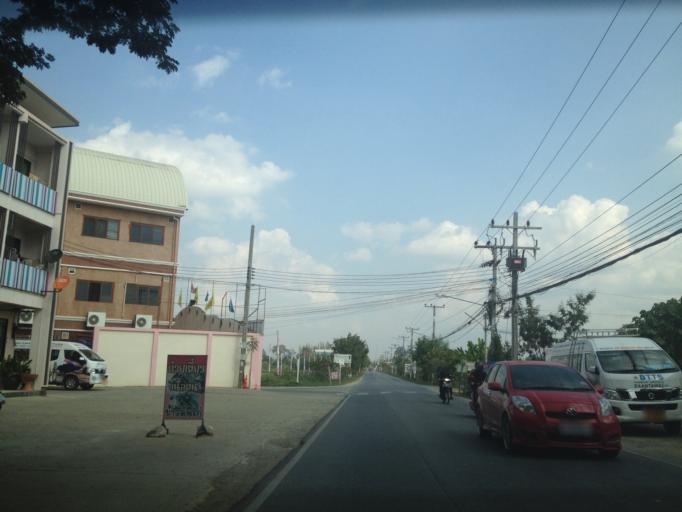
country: TH
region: Chiang Mai
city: Saraphi
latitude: 18.7070
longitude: 99.0265
